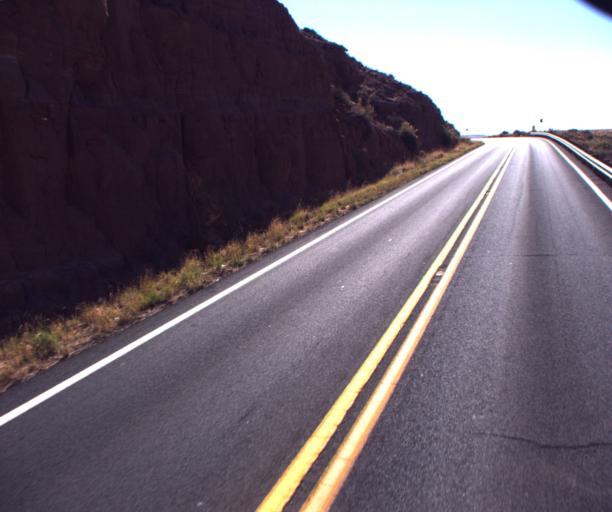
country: US
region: Arizona
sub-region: Coconino County
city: Tuba City
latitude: 36.1099
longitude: -111.2190
